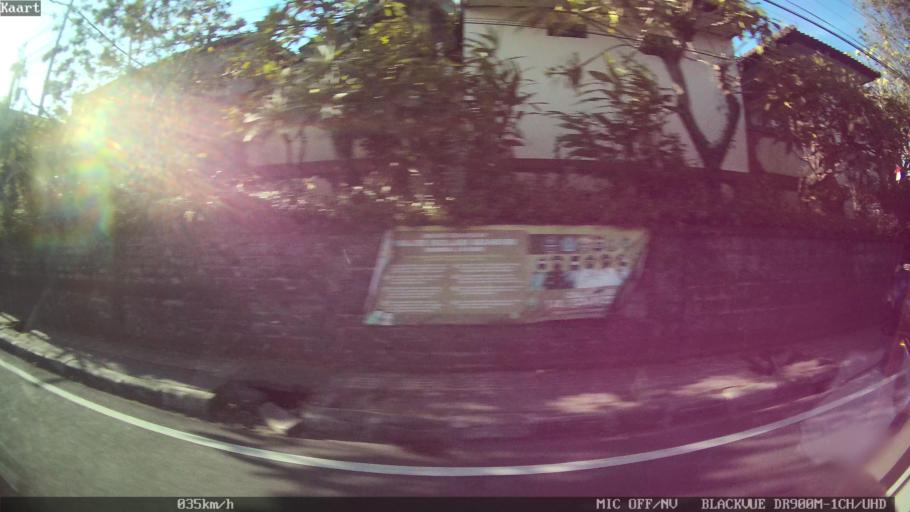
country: ID
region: Bali
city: Banjar Kertasari
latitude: -8.6322
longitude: 115.2035
